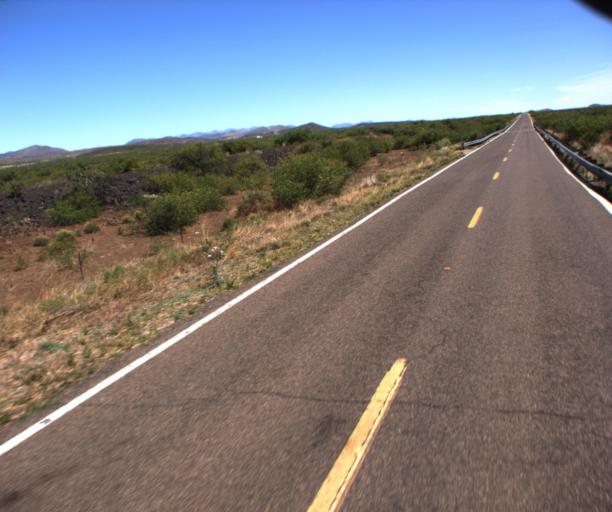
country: US
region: Arizona
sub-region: Cochise County
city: Douglas
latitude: 31.4743
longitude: -109.3551
